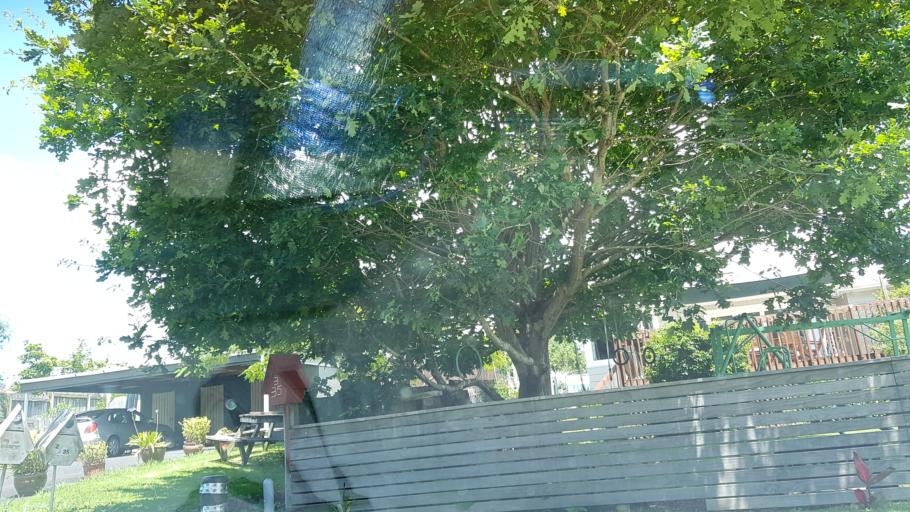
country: NZ
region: Auckland
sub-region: Auckland
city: North Shore
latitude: -36.7875
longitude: 174.6959
